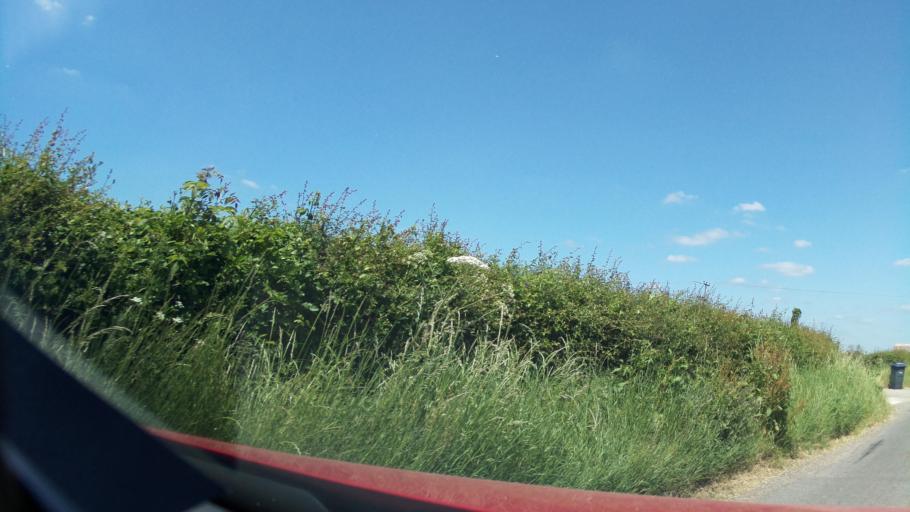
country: GB
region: England
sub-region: Wiltshire
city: Royal Wootton Bassett
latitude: 51.5026
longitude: -1.9101
